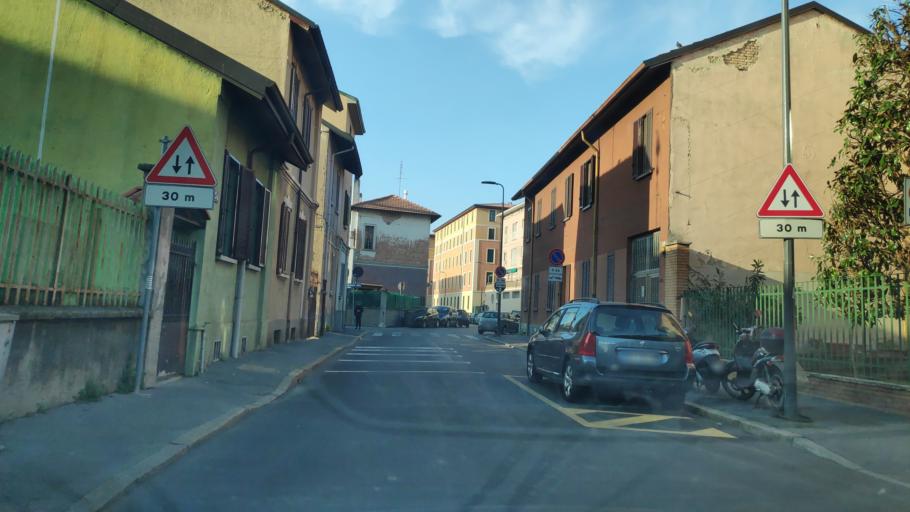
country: IT
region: Lombardy
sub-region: Citta metropolitana di Milano
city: Cesano Boscone
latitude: 45.4679
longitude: 9.0907
